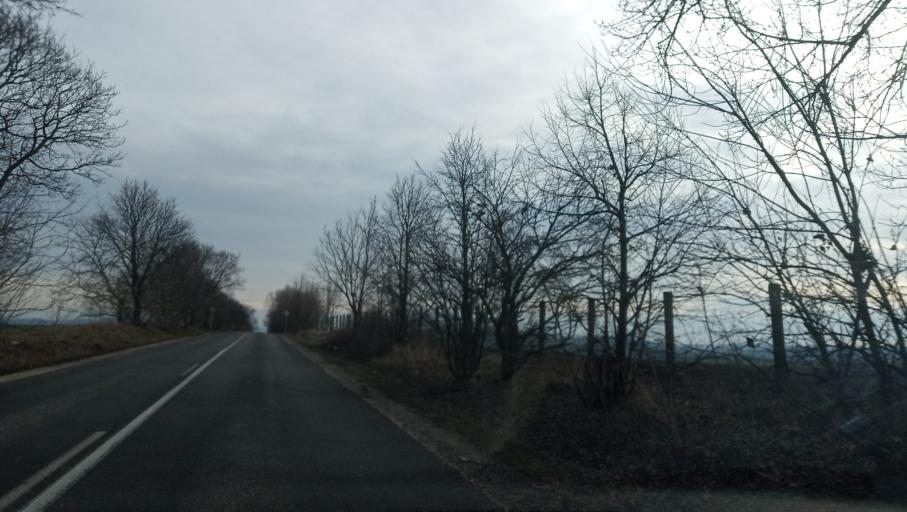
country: HU
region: Pest
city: Kosd
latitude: 47.7686
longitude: 19.1906
